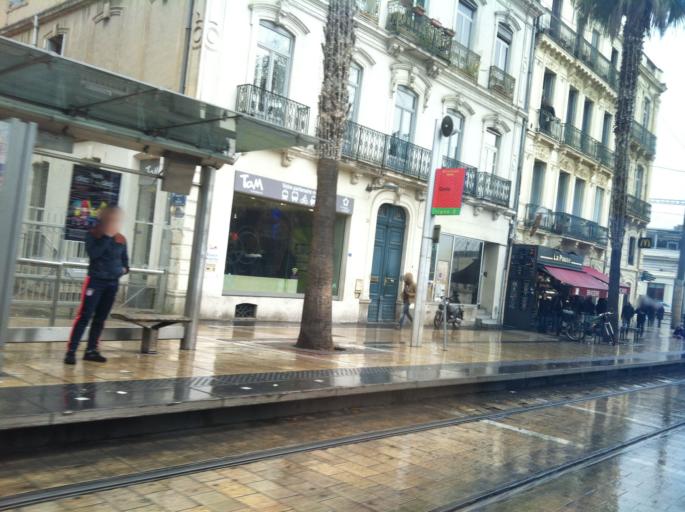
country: FR
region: Languedoc-Roussillon
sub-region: Departement de l'Herault
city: Montpellier
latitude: 43.6057
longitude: 3.8803
